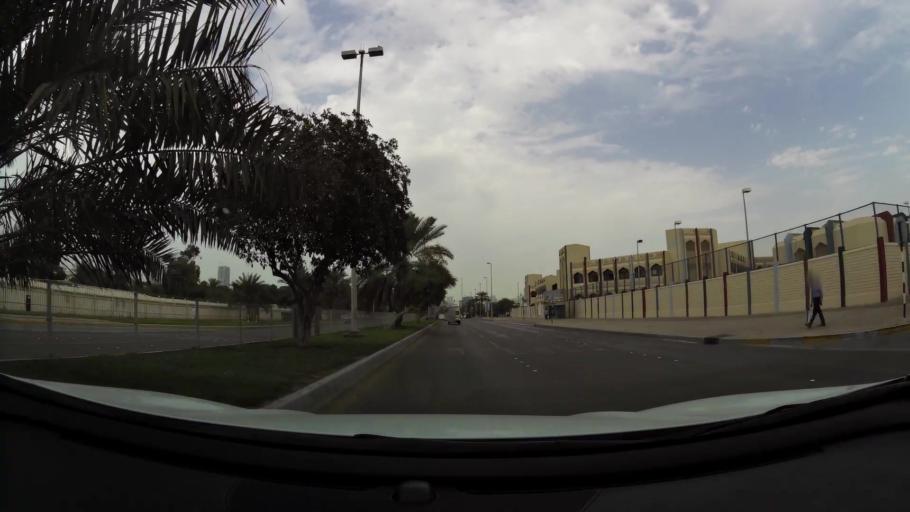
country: AE
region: Abu Dhabi
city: Abu Dhabi
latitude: 24.4667
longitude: 54.3542
